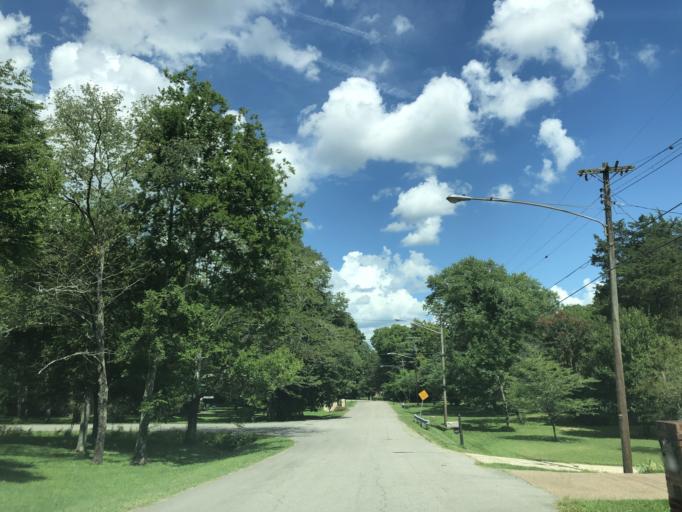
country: US
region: Tennessee
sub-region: Davidson County
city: Oak Hill
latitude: 36.0791
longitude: -86.7337
